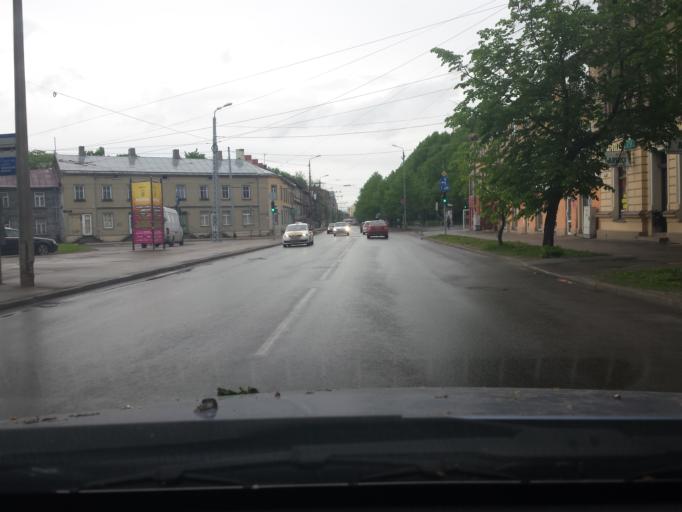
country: LV
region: Riga
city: Riga
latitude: 56.9558
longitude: 24.1531
